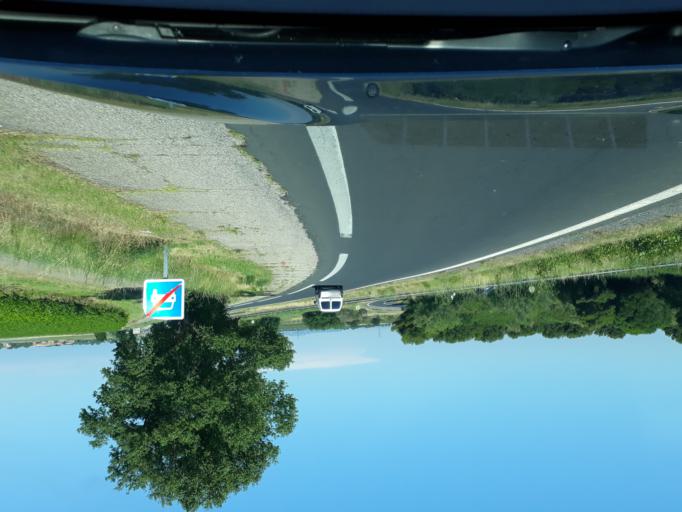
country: FR
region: Languedoc-Roussillon
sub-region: Departement de l'Herault
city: Le Cap d'Agde
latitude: 43.3073
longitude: 3.5088
